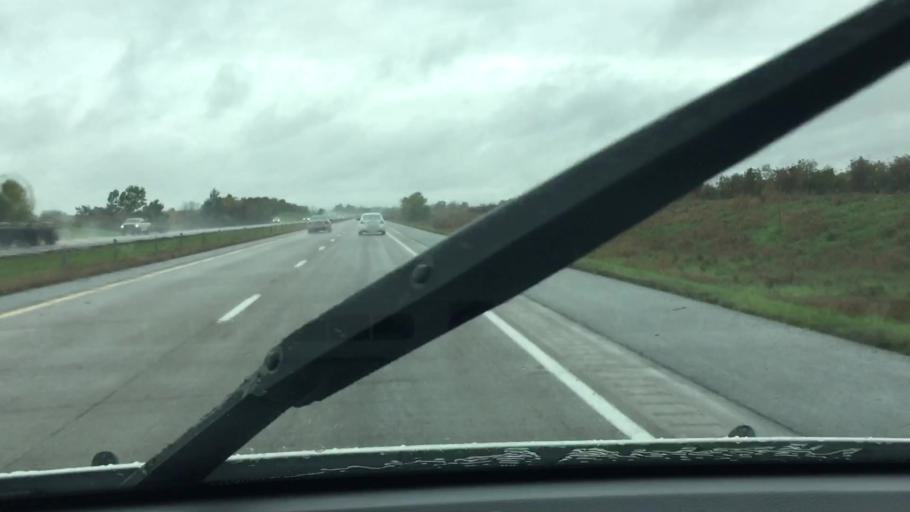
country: US
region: Iowa
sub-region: Poweshiek County
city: Brooklyn
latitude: 41.6955
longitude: -92.5197
